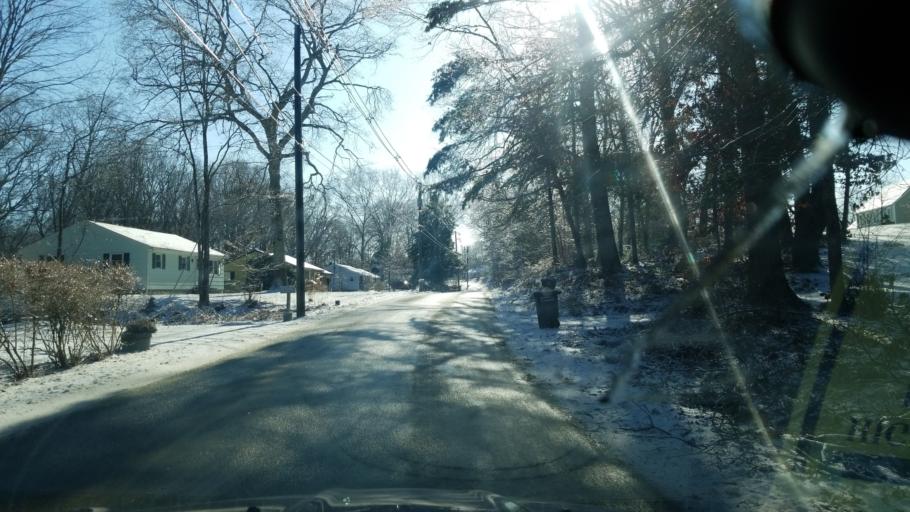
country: US
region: Connecticut
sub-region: Windham County
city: East Brooklyn
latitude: 41.8237
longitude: -71.9302
